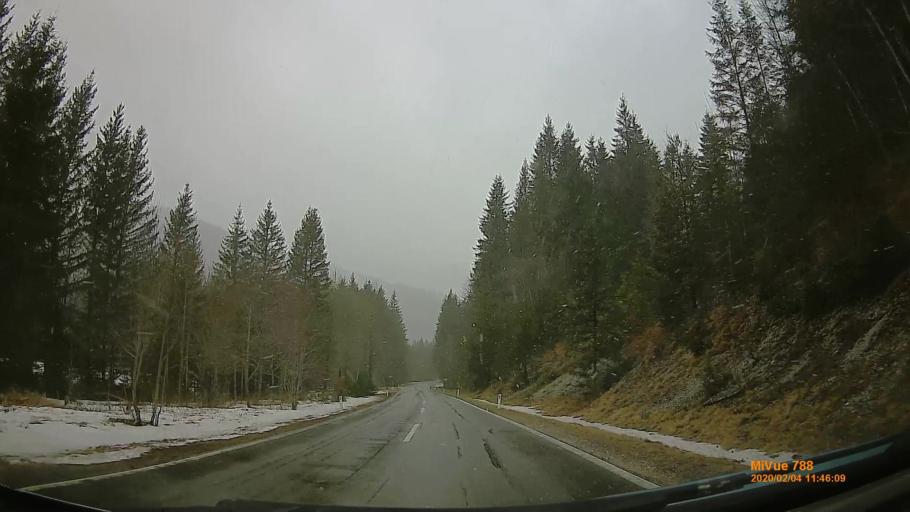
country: AT
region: Styria
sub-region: Politischer Bezirk Bruck-Muerzzuschlag
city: Muerzsteg
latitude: 47.6988
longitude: 15.4807
